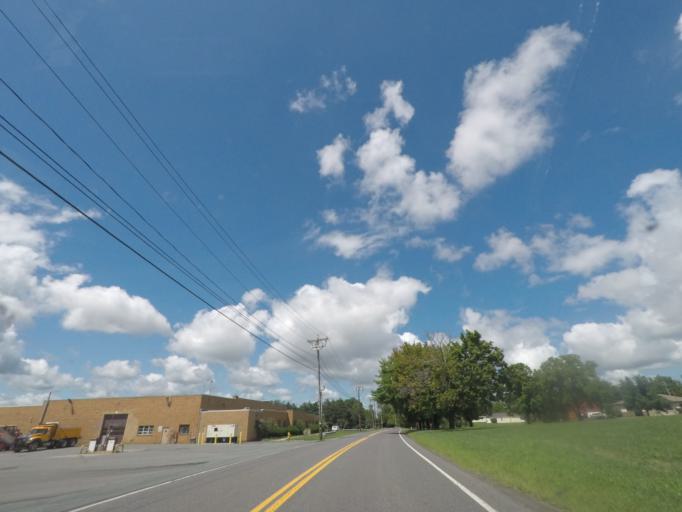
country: US
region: New York
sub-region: Rensselaer County
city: Wynantskill
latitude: 42.6866
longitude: -73.6813
